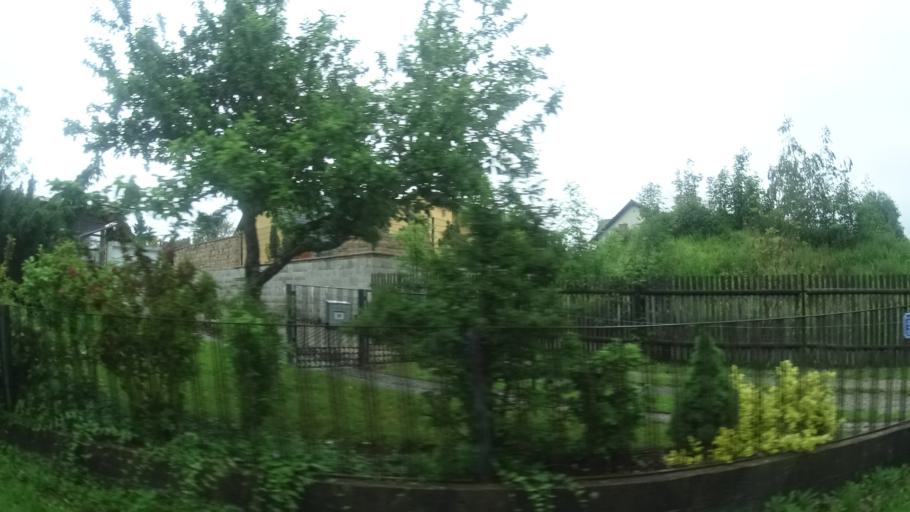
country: DE
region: Thuringia
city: Langewiesen
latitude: 50.6766
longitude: 10.9628
